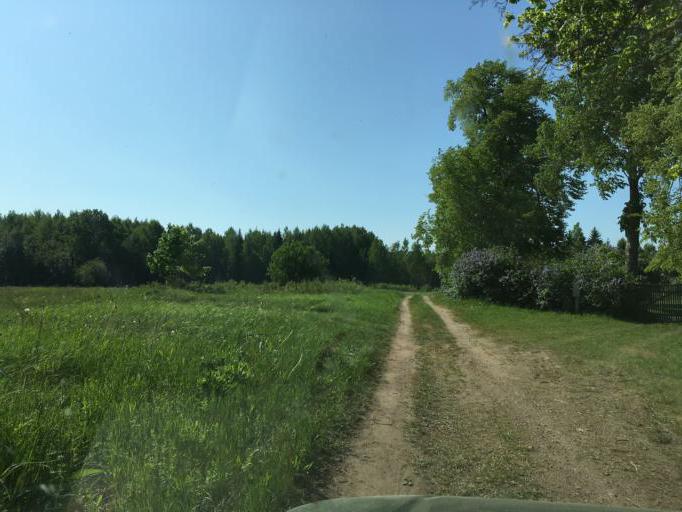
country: LV
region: Ventspils
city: Ventspils
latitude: 57.4810
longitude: 21.7629
